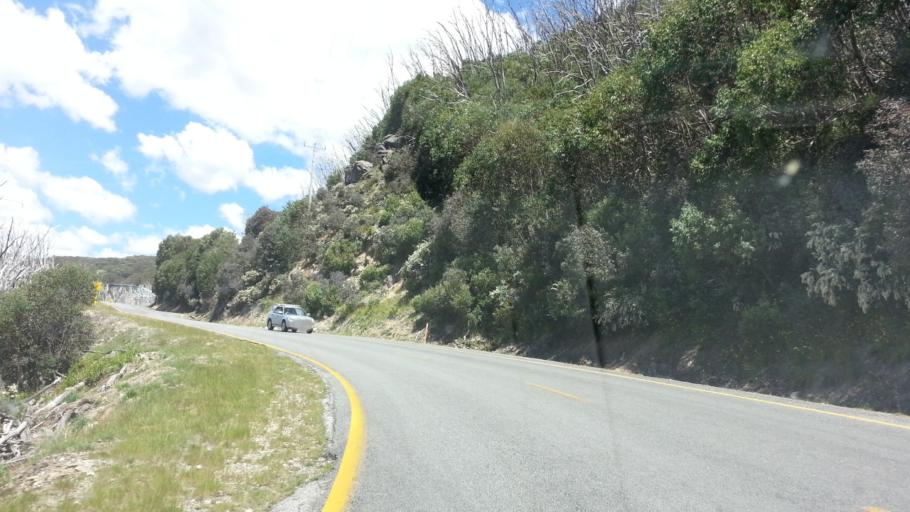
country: AU
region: Victoria
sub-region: Alpine
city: Mount Beauty
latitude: -36.8561
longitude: 147.2736
